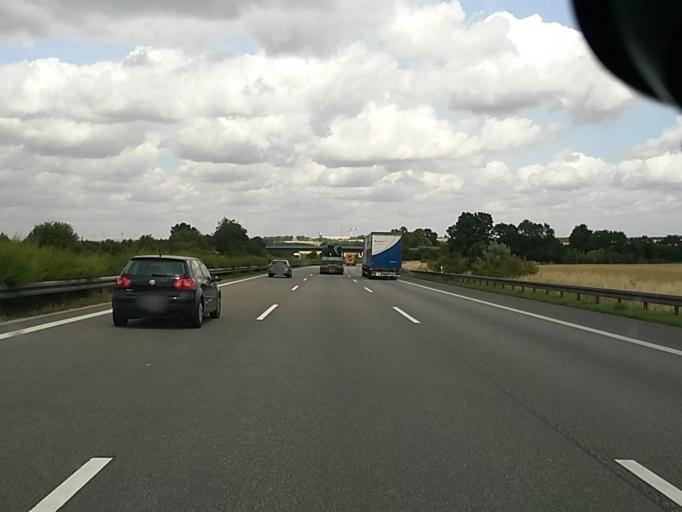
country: DE
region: Thuringia
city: Walpernhain
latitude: 51.0436
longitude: 11.9415
